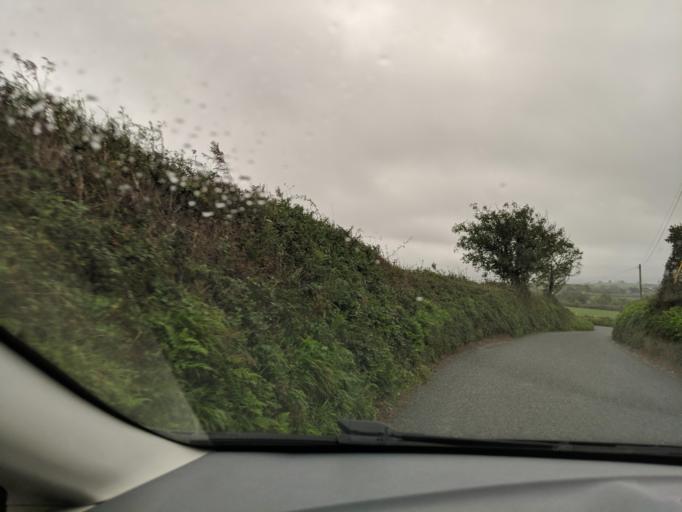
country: GB
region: England
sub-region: Cornwall
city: Saltash
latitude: 50.4504
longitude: -4.2381
